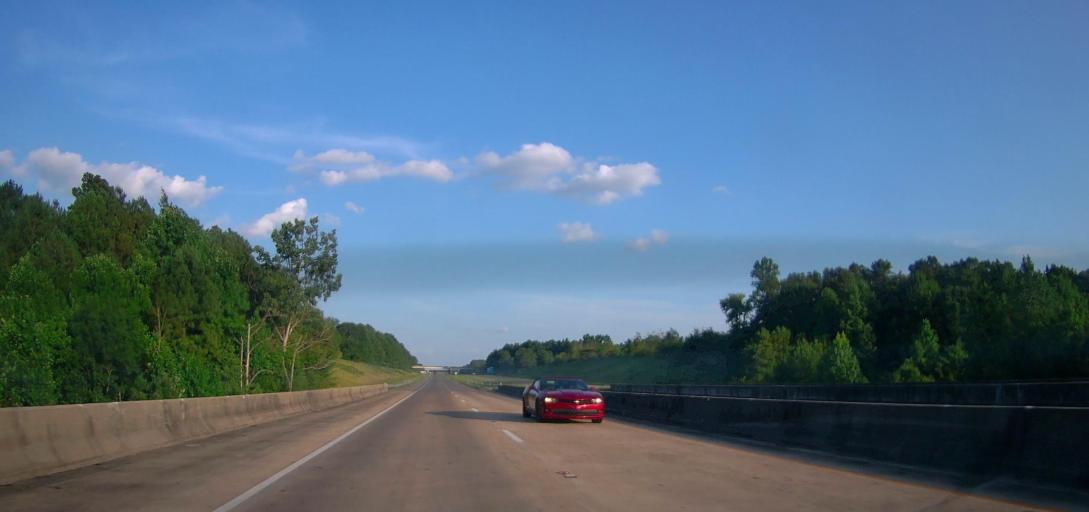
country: US
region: Alabama
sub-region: Walker County
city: Carbon Hill
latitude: 33.8850
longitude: -87.4498
